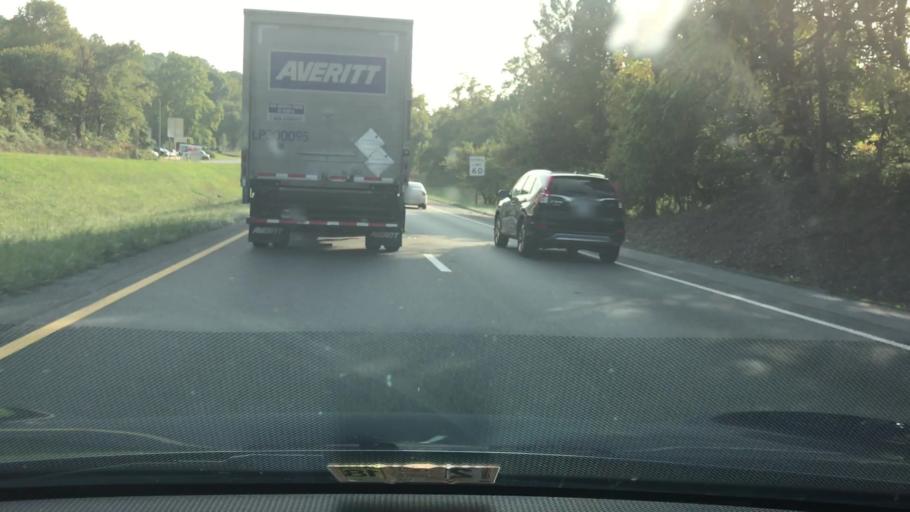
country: US
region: Virginia
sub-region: Botetourt County
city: Laymantown
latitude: 37.3445
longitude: -79.8466
